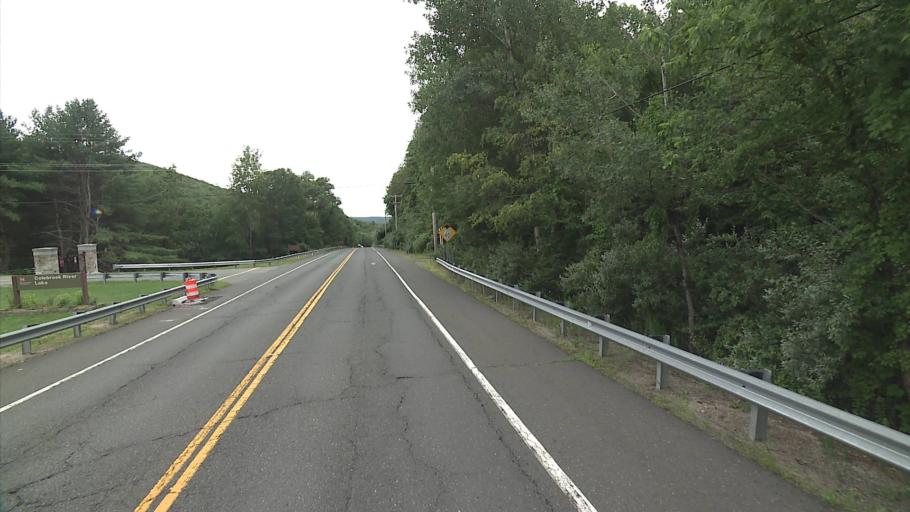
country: US
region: Connecticut
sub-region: Litchfield County
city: Winsted
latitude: 41.9984
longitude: -73.0471
